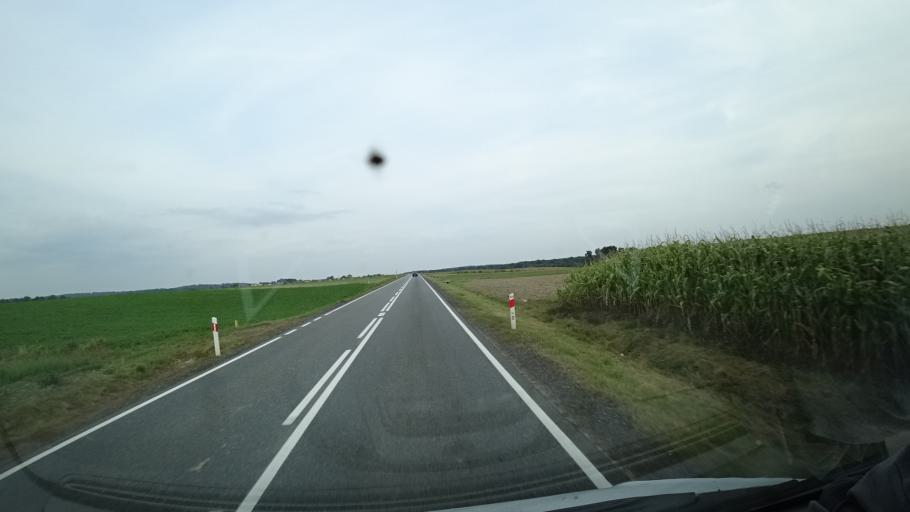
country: PL
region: Silesian Voivodeship
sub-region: Powiat gliwicki
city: Rudziniec
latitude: 50.3863
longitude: 18.4100
